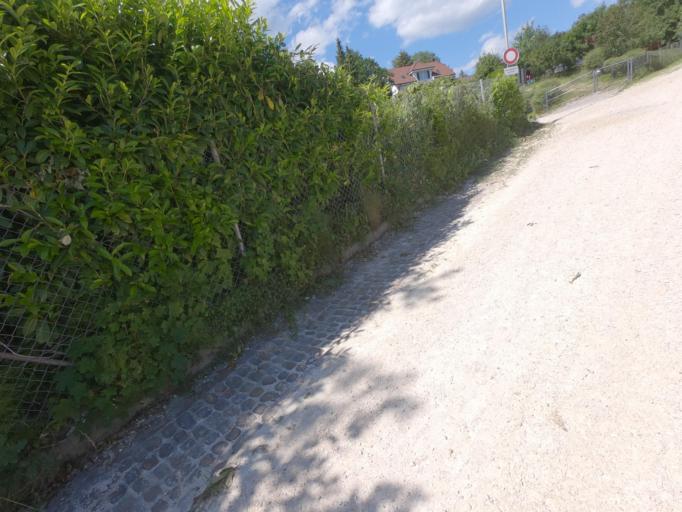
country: CH
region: Solothurn
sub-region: Bezirk Solothurn
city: Solothurn
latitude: 47.2162
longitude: 7.5340
